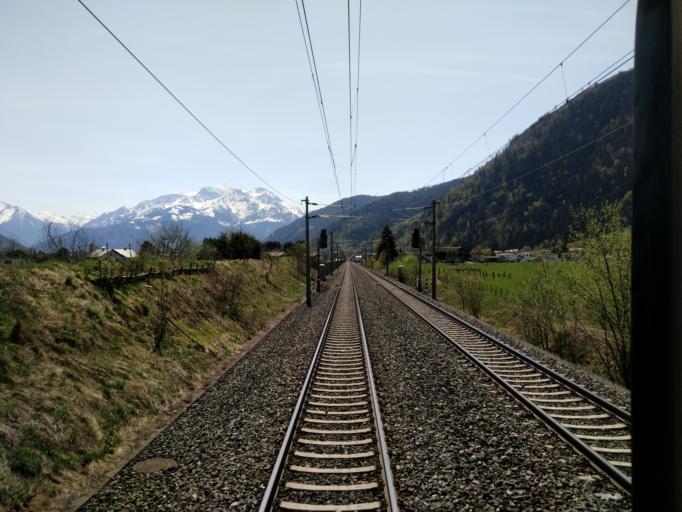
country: AT
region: Salzburg
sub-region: Politischer Bezirk Zell am See
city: Maishofen
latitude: 47.3541
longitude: 12.8075
